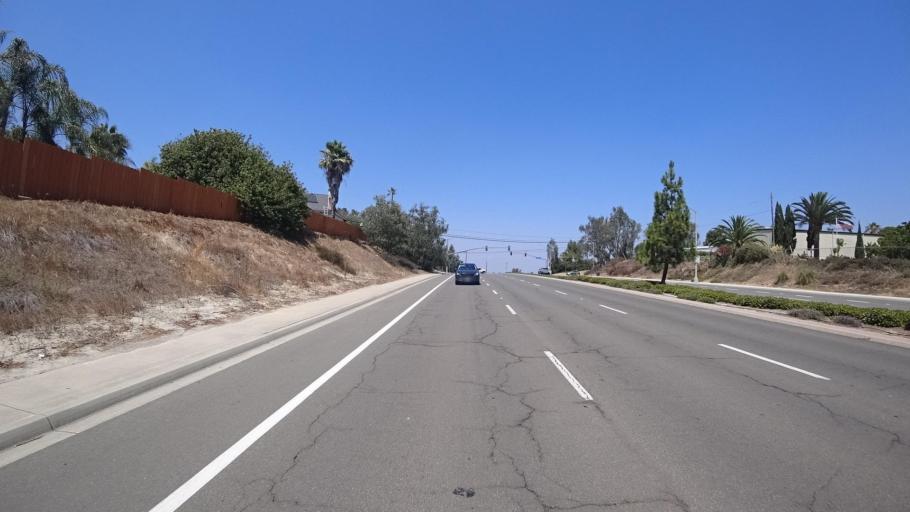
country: US
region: California
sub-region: San Diego County
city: Vista
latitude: 33.1770
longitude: -117.2538
